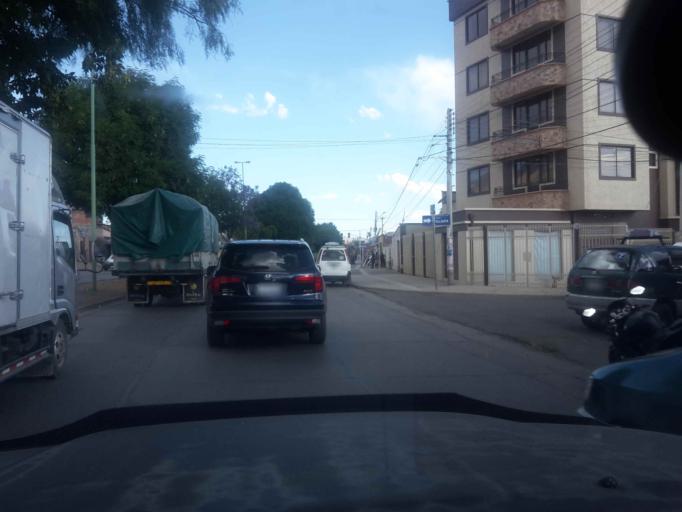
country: BO
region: Cochabamba
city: Cochabamba
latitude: -17.3531
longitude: -66.1814
